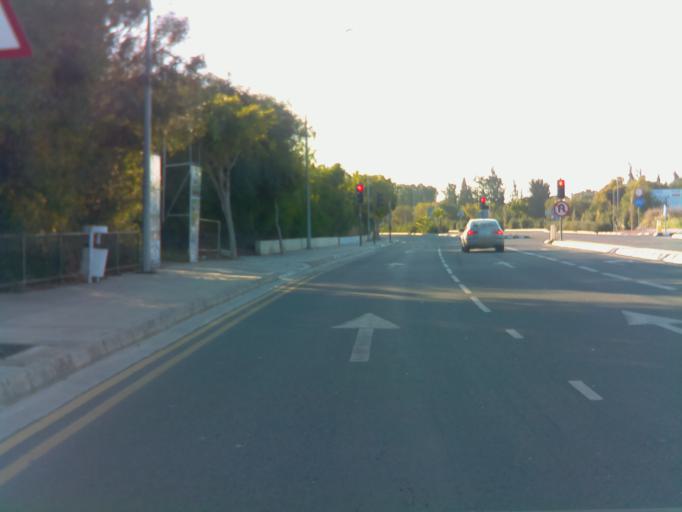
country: CY
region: Pafos
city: Paphos
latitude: 34.7570
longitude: 32.4247
